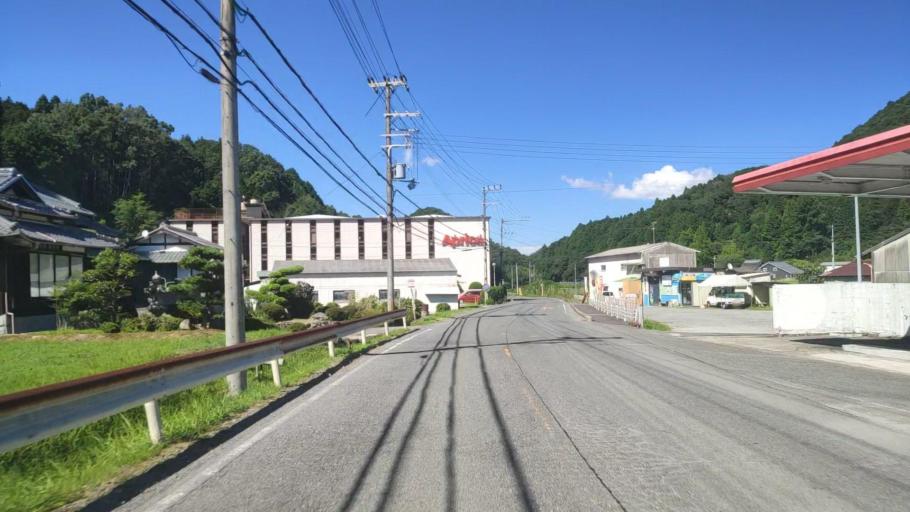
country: JP
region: Nara
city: Haibara-akanedai
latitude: 34.5781
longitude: 135.9671
